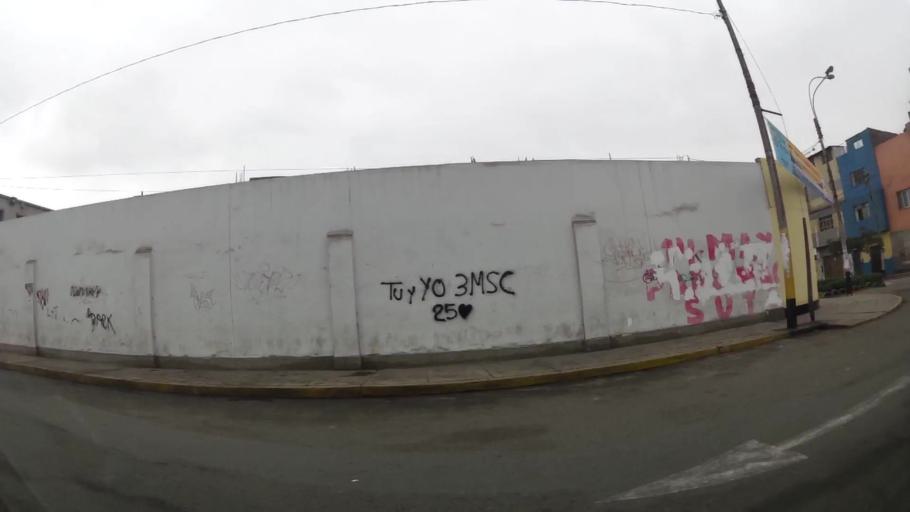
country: PE
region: Lima
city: Lima
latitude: -12.0602
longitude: -77.0529
